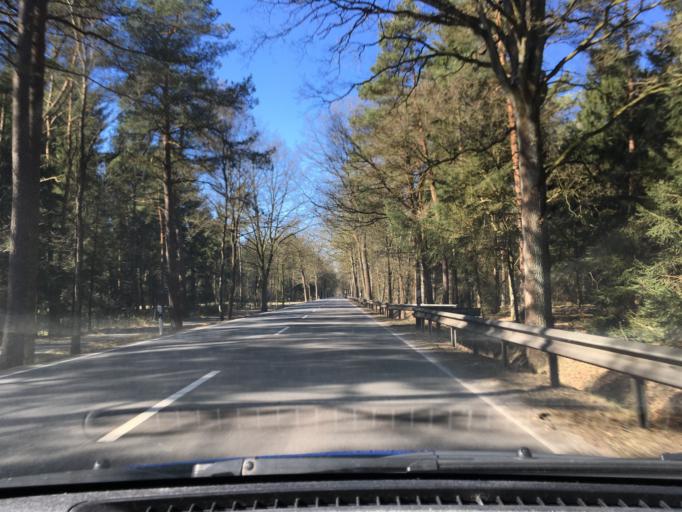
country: DE
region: Lower Saxony
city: Hemslingen
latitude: 53.0904
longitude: 9.5597
